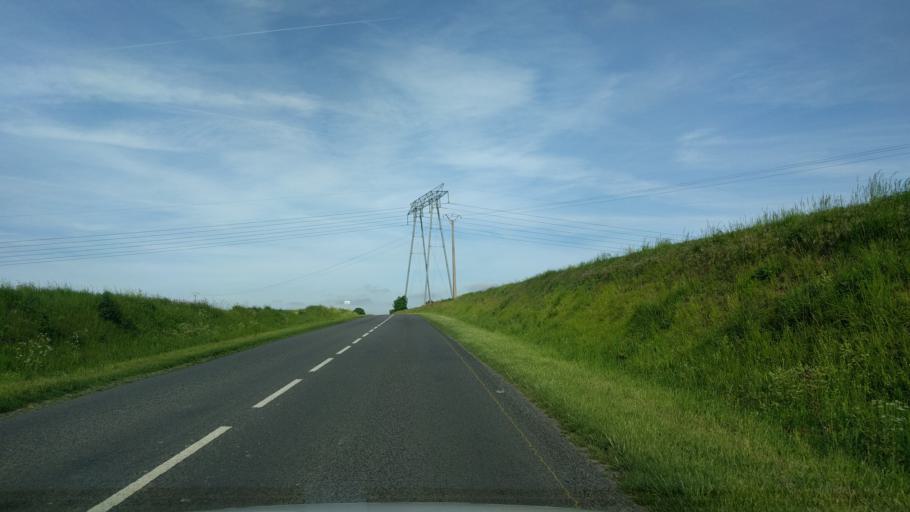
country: FR
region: Picardie
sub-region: Departement de la Somme
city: Peronne
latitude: 49.9586
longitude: 2.8721
